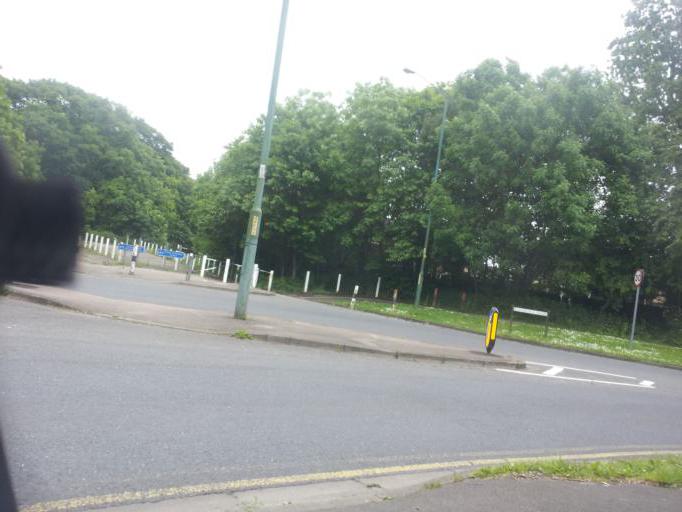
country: GB
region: England
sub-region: Kent
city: Boxley
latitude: 51.3384
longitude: 0.5492
